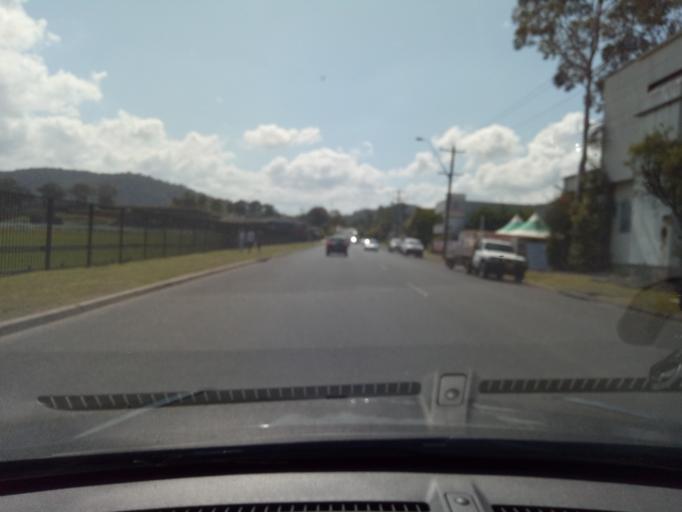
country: AU
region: New South Wales
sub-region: Gosford Shire
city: Gosford
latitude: -33.4244
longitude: 151.3278
